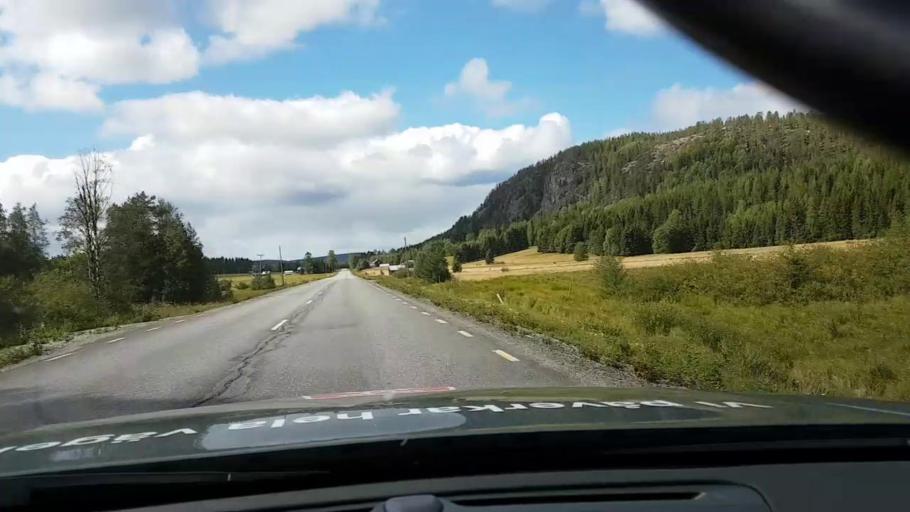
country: SE
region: Vaesternorrland
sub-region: OErnskoeldsviks Kommun
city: Bredbyn
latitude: 63.5267
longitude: 18.0209
